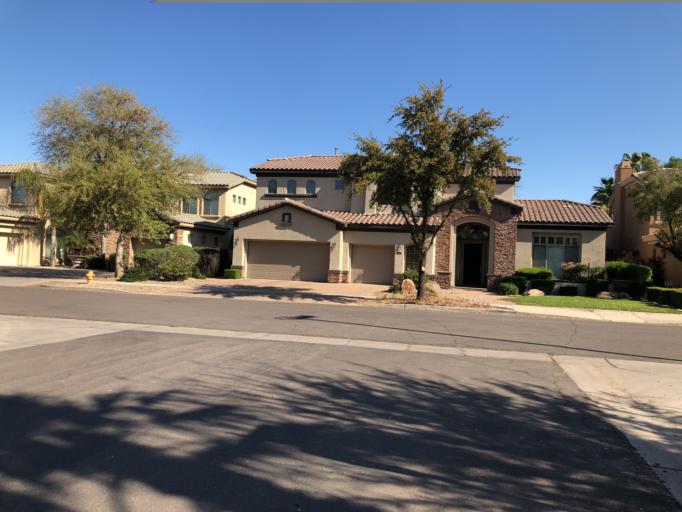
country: US
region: Arizona
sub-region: Maricopa County
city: Queen Creek
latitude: 33.2696
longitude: -111.6879
